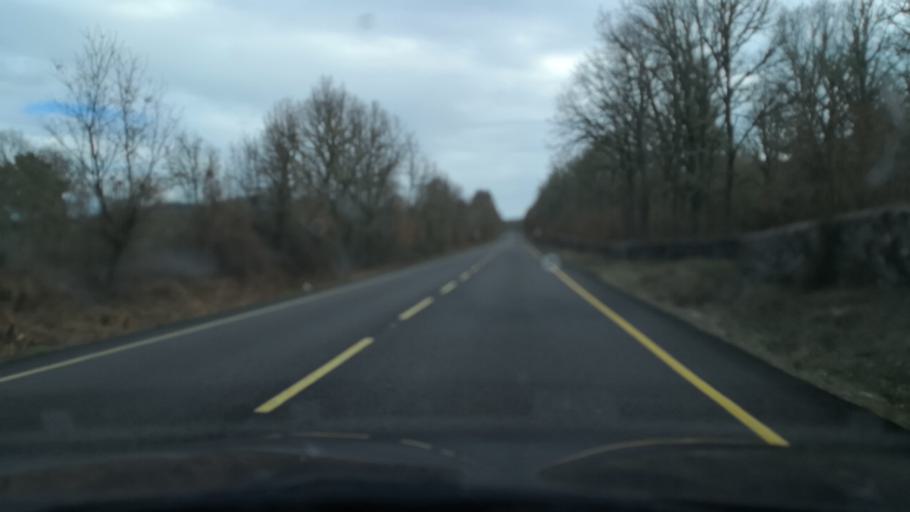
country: ES
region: Castille and Leon
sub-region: Provincia de Salamanca
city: Villasrubias
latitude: 40.3197
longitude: -6.6479
